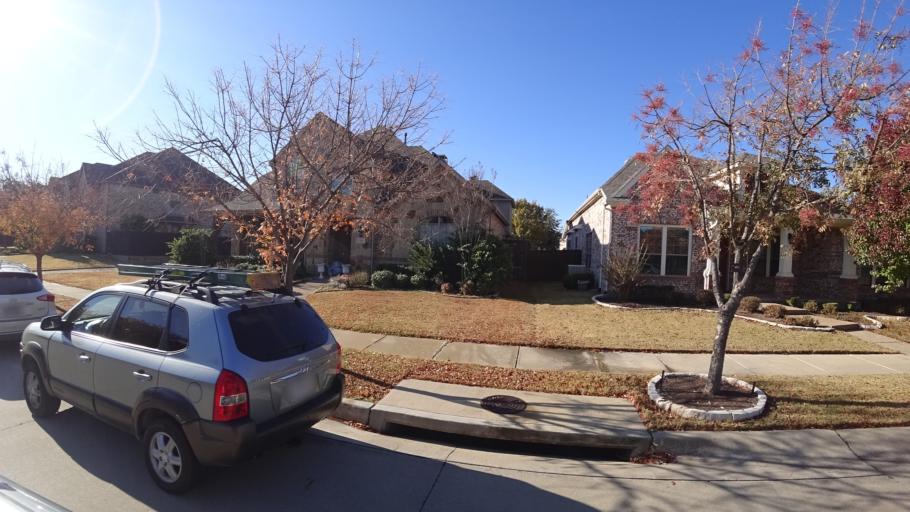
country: US
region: Texas
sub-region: Denton County
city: The Colony
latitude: 33.0438
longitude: -96.9148
